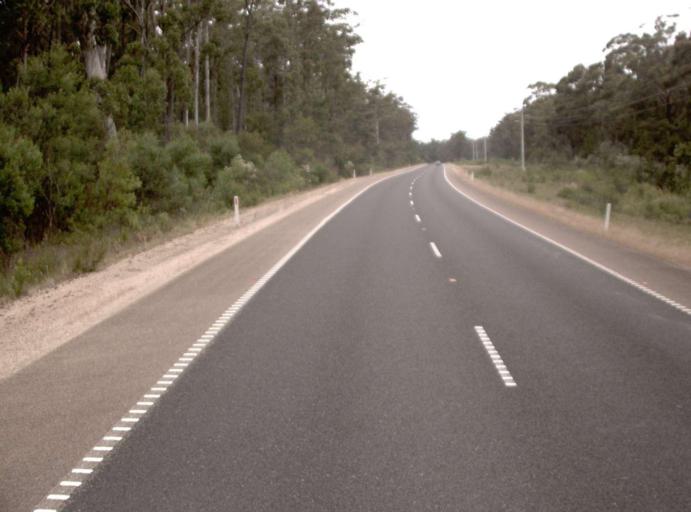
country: AU
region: Victoria
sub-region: East Gippsland
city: Lakes Entrance
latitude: -37.7128
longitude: 148.0738
